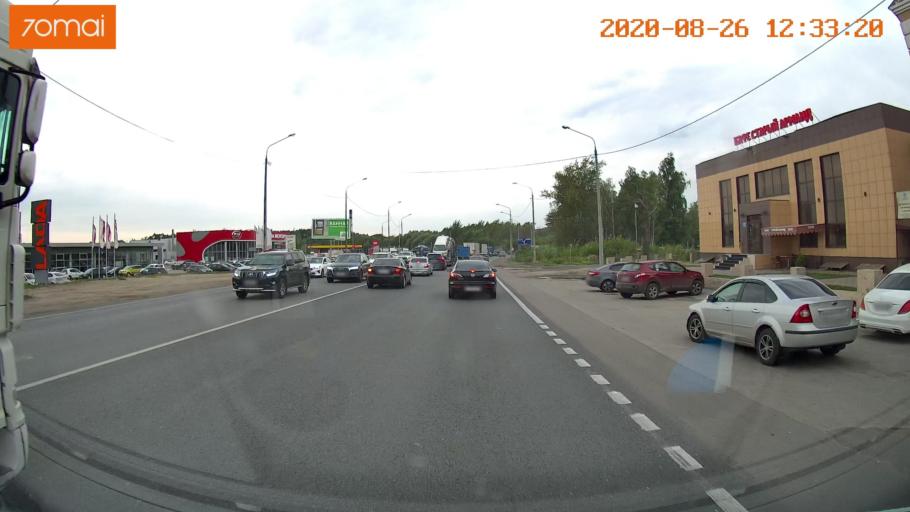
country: RU
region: Rjazan
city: Ryazan'
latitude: 54.5815
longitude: 39.7776
